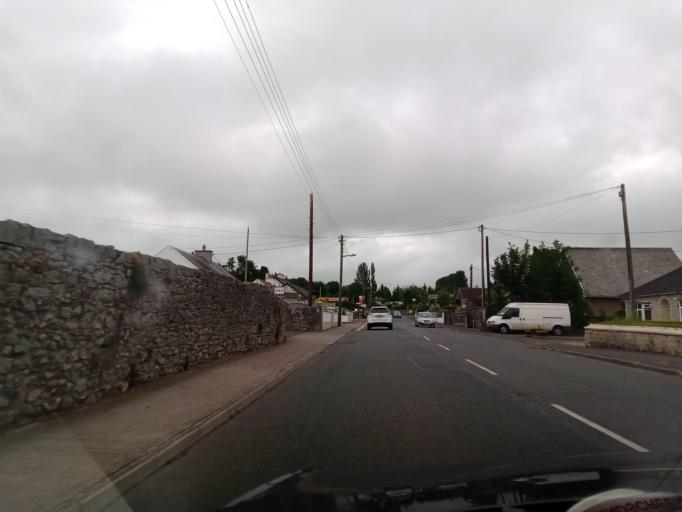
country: IE
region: Leinster
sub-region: Laois
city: Abbeyleix
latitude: 52.9132
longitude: -7.3459
